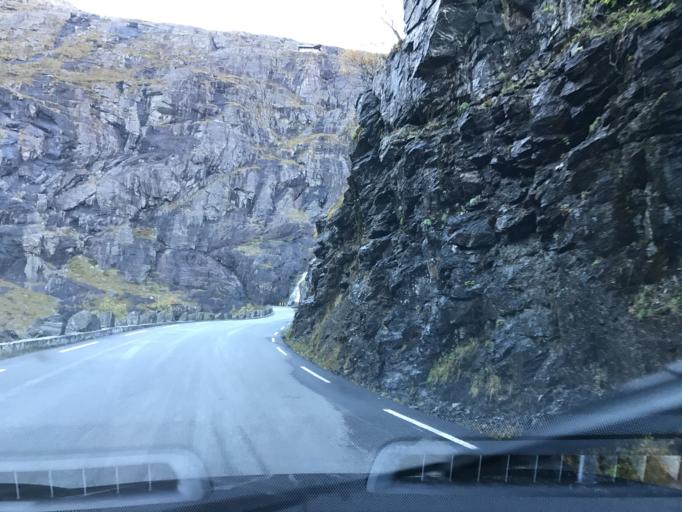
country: NO
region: More og Romsdal
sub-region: Rauma
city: Andalsnes
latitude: 62.4581
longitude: 7.6726
